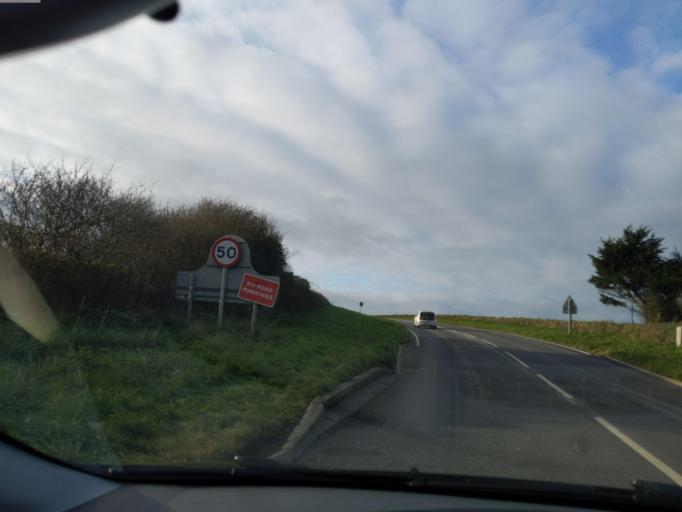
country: GB
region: England
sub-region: Cornwall
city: Padstow
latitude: 50.5136
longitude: -4.9443
